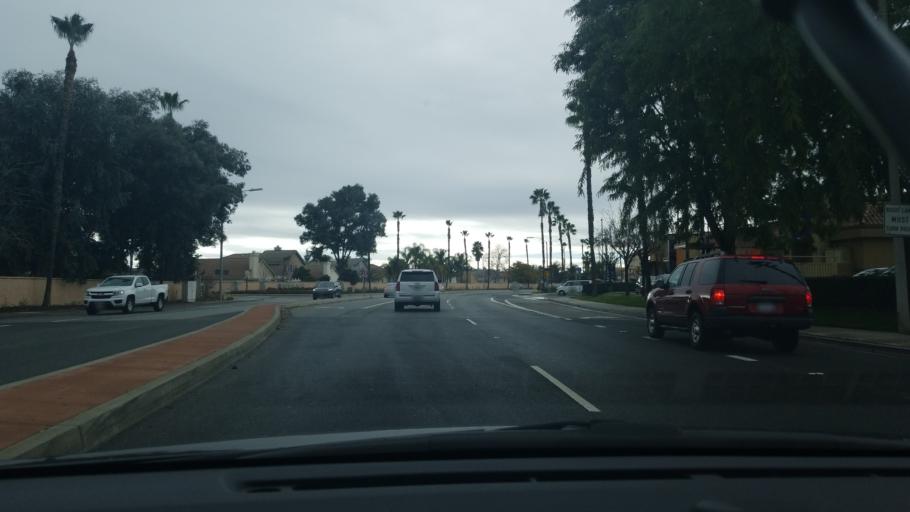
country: US
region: California
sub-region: Riverside County
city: Sun City
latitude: 33.6840
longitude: -117.1673
